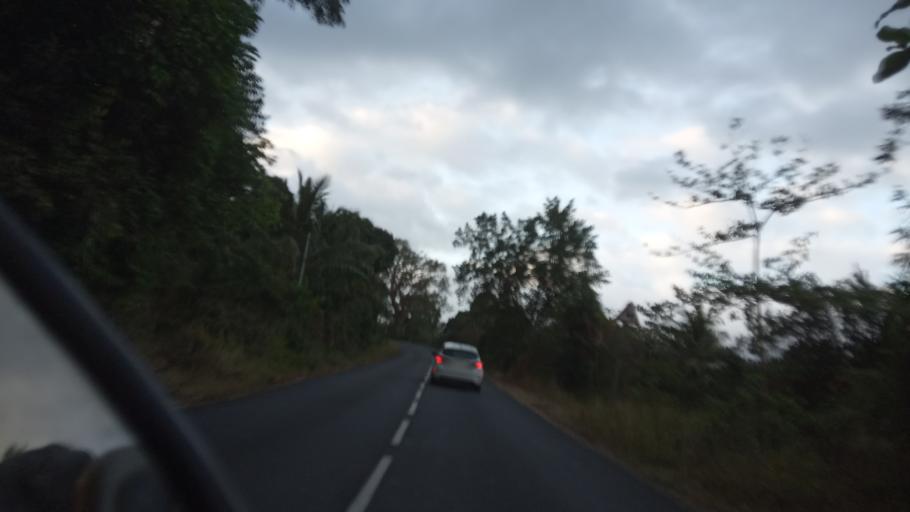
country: YT
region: Chirongui
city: Chirongui
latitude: -12.9317
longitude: 45.1234
